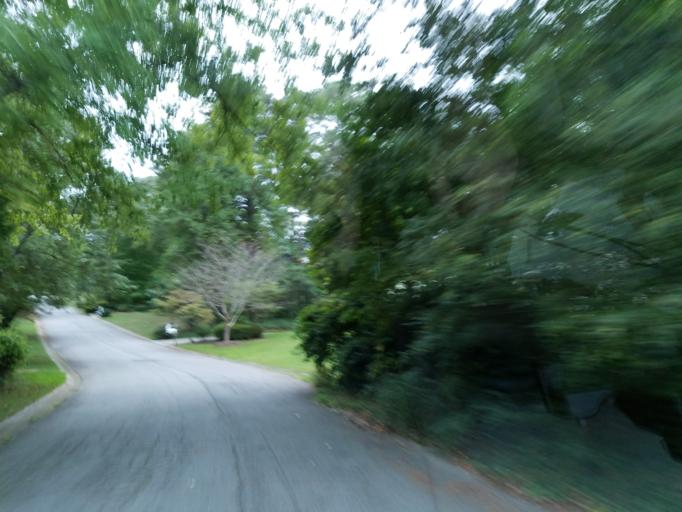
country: US
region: Georgia
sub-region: Fulton County
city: Sandy Springs
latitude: 33.9597
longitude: -84.4368
